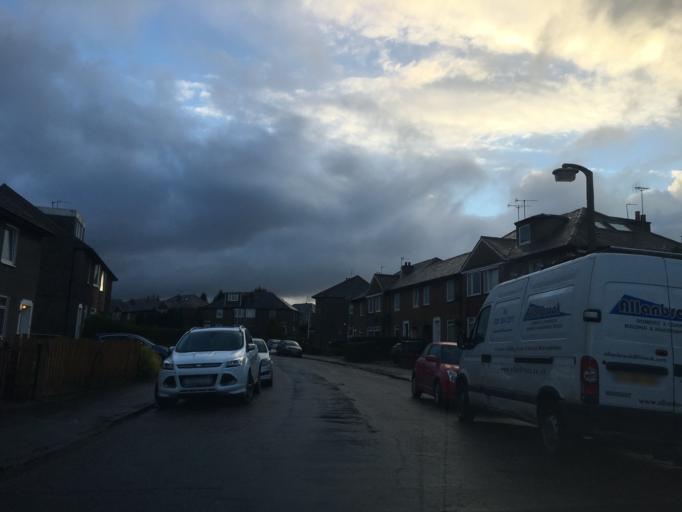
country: GB
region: Scotland
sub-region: Edinburgh
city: Colinton
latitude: 55.9349
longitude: -3.2802
